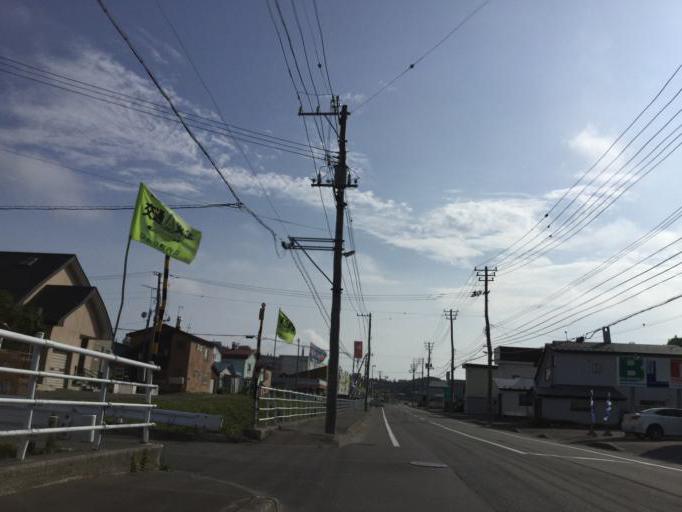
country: JP
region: Hokkaido
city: Wakkanai
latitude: 45.3886
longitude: 141.6771
